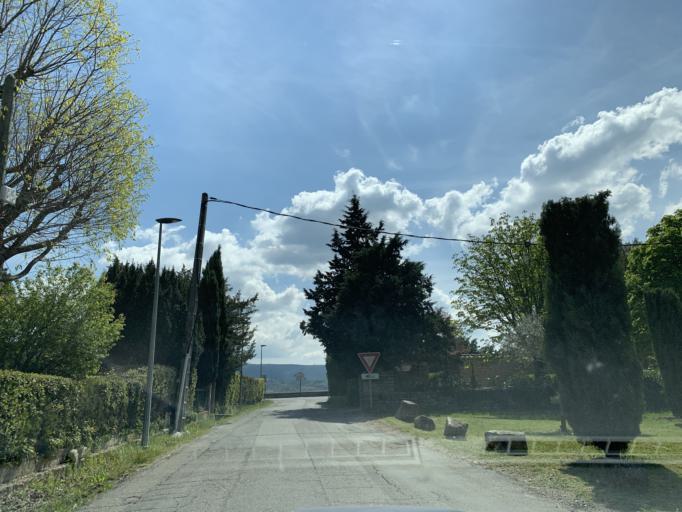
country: FR
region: Provence-Alpes-Cote d'Azur
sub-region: Departement du Vaucluse
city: Goult
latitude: 43.8638
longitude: 5.2485
